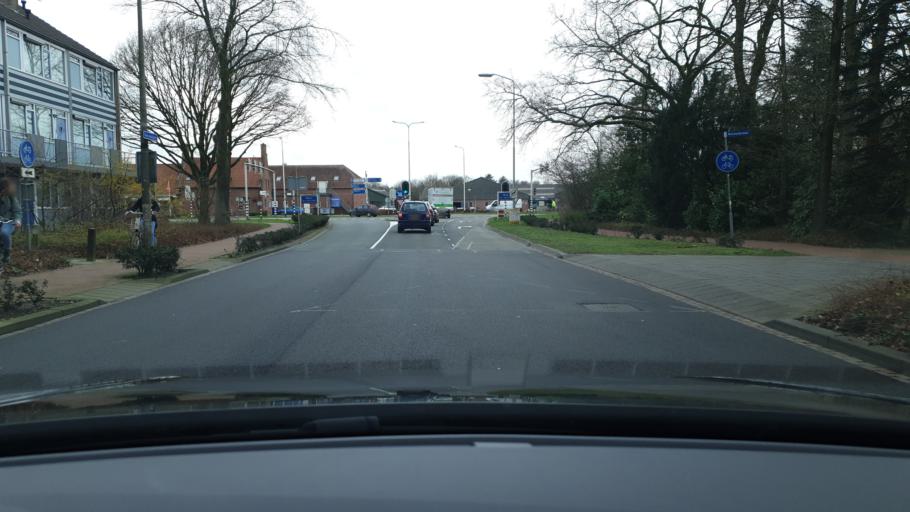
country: NL
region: North Brabant
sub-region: Gemeente Dongen
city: Dongen
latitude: 51.5883
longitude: 4.9045
